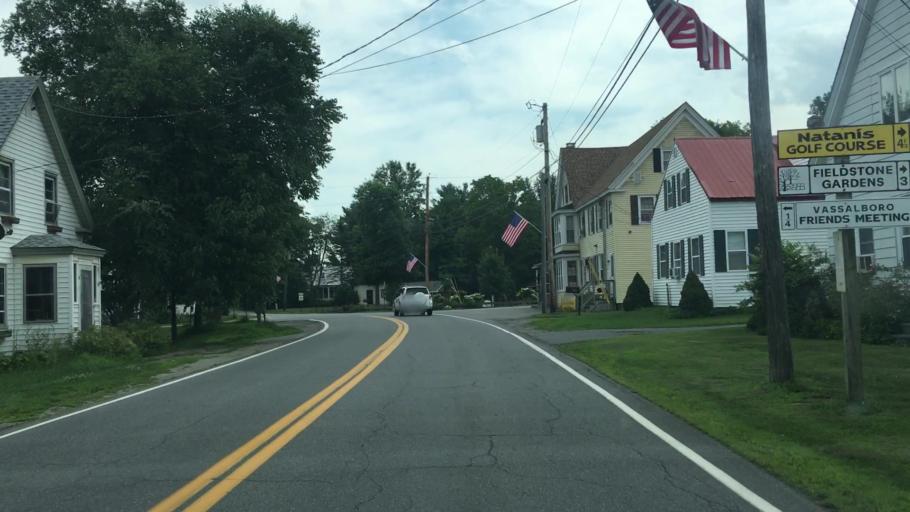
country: US
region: Maine
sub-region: Kennebec County
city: Vassalboro
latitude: 44.4484
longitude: -69.6065
